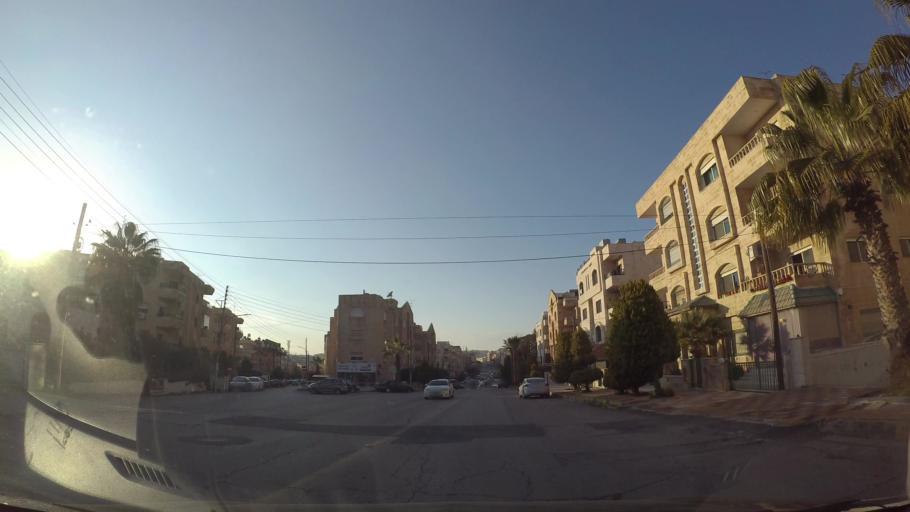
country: JO
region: Amman
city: Al Jubayhah
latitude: 31.9752
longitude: 35.8730
